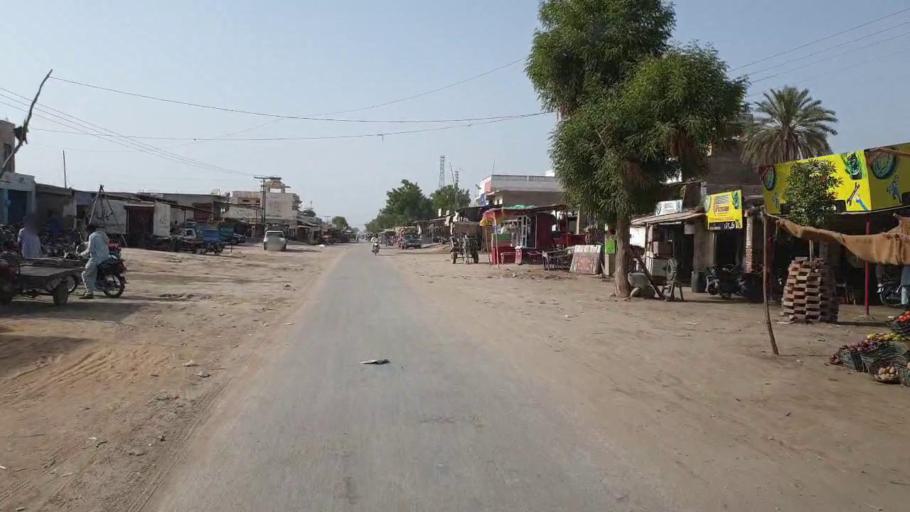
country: PK
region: Sindh
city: Sanghar
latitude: 26.2694
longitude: 68.9297
